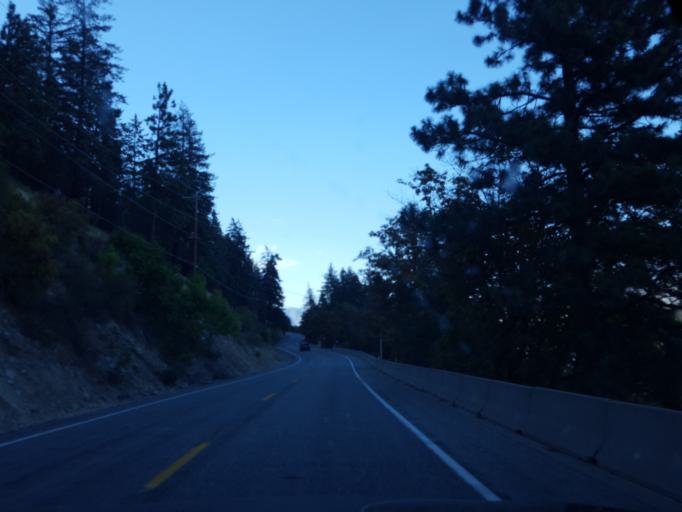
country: US
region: Washington
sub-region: Chelan County
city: Granite Falls
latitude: 47.8953
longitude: -120.2152
